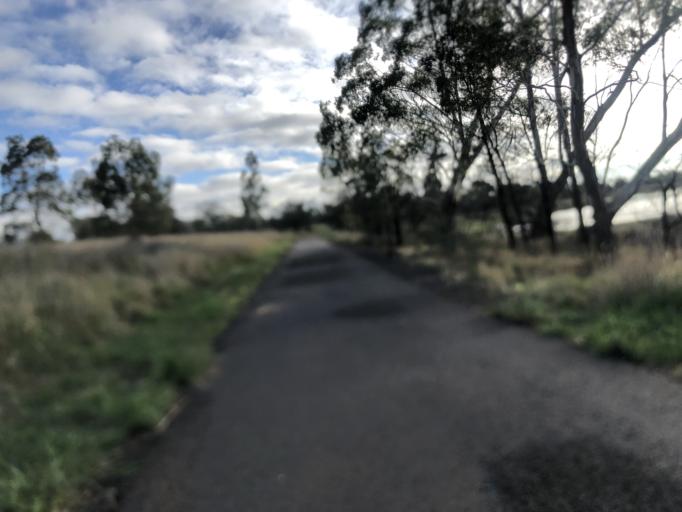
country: AU
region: New South Wales
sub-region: Orange Municipality
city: Orange
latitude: -33.3283
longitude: 149.0859
